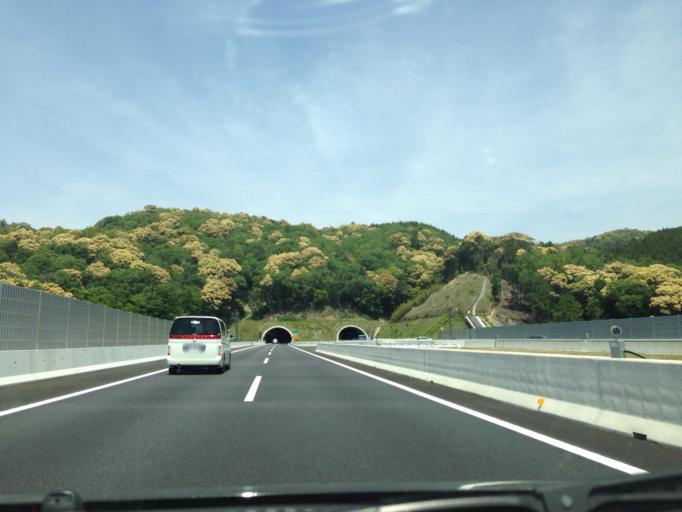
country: JP
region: Aichi
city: Okazaki
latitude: 34.9433
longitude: 137.2580
